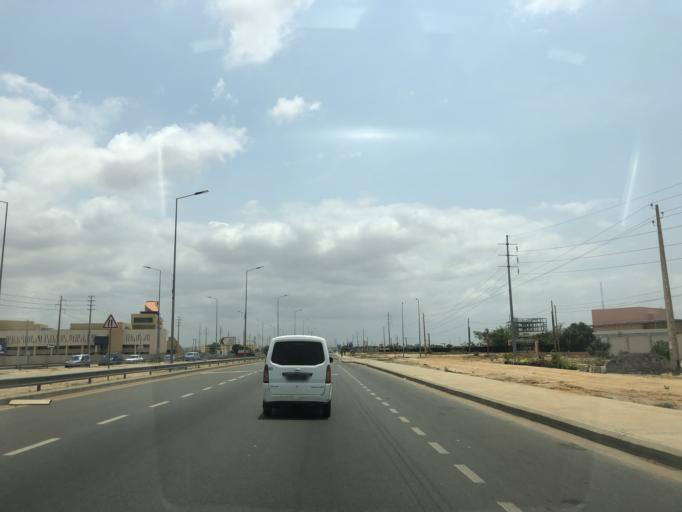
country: AO
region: Luanda
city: Luanda
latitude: -8.9589
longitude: 13.2572
